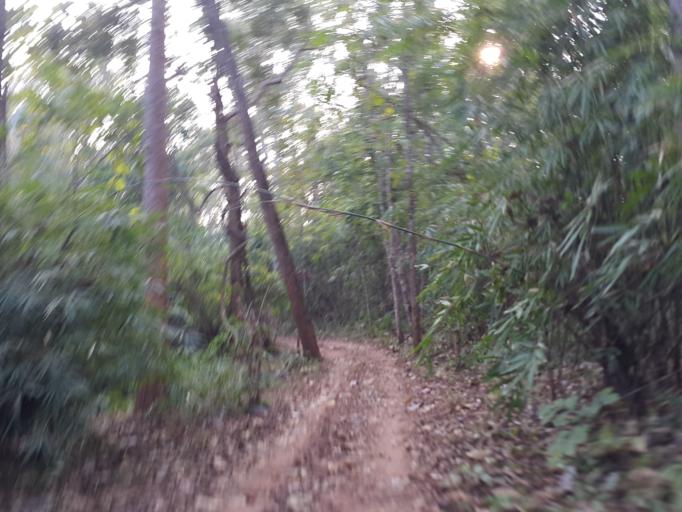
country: TH
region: Lamphun
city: Li
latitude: 17.6179
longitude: 98.9056
